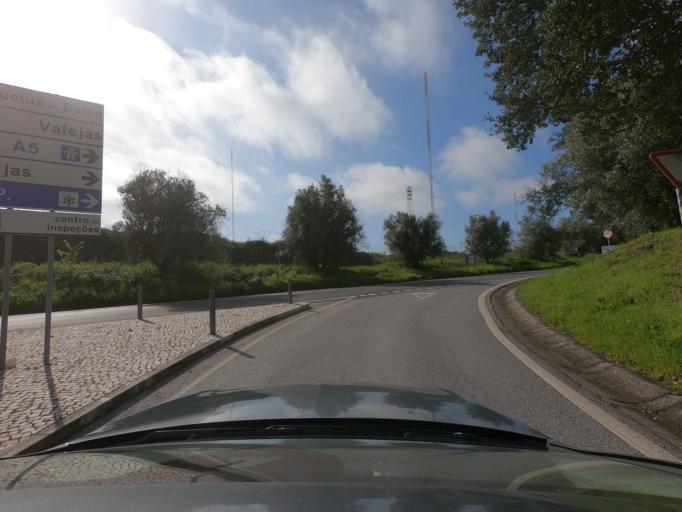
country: PT
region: Lisbon
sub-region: Oeiras
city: Quejas
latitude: 38.7271
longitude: -9.2702
